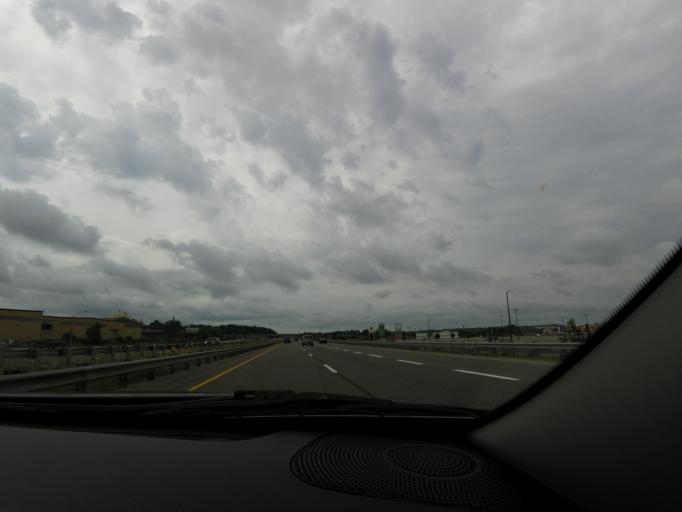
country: CA
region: Ontario
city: Orillia
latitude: 44.6317
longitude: -79.4321
